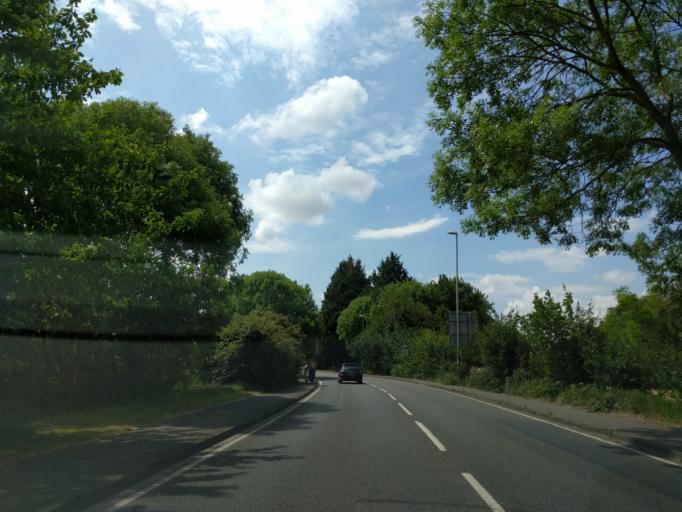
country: GB
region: England
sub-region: Cambridgeshire
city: Fulbourn
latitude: 52.1952
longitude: 0.1831
